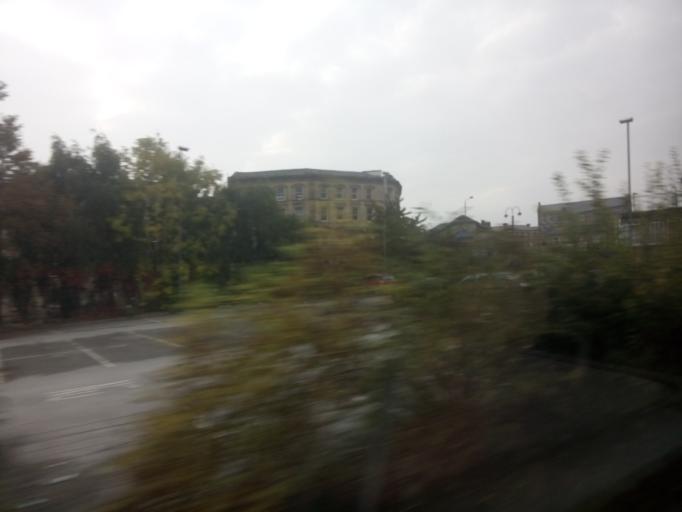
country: GB
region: England
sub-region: Kirklees
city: Dewsbury
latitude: 53.6926
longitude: -1.6324
